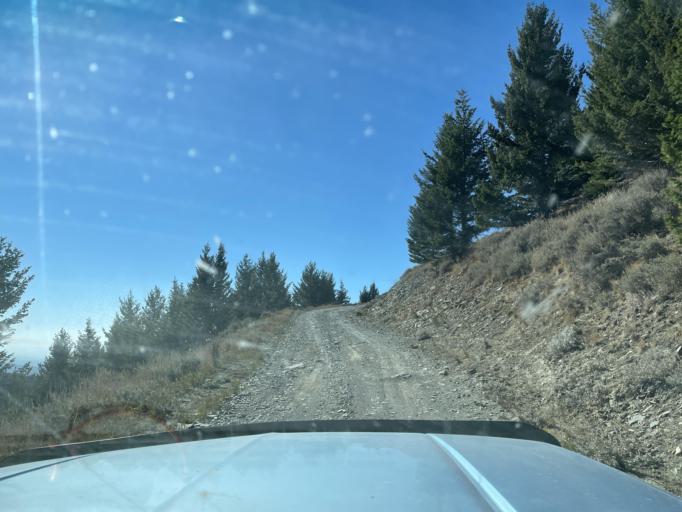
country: US
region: Montana
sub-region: Broadwater County
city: Townsend
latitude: 46.4979
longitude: -111.2614
